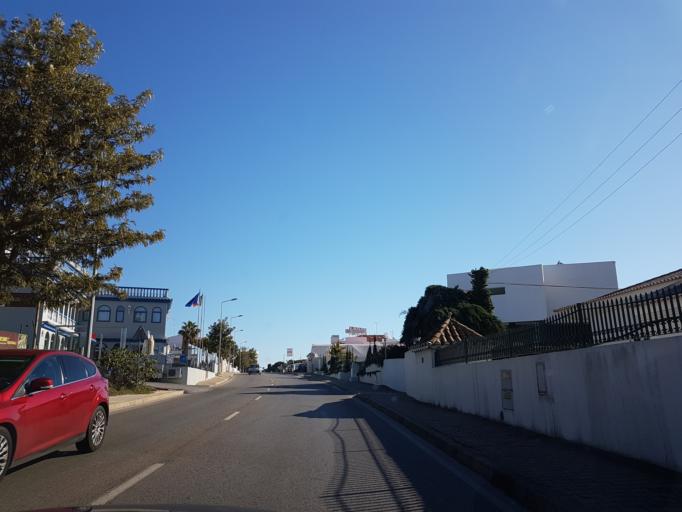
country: PT
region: Faro
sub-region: Albufeira
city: Albufeira
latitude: 37.0913
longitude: -8.2143
